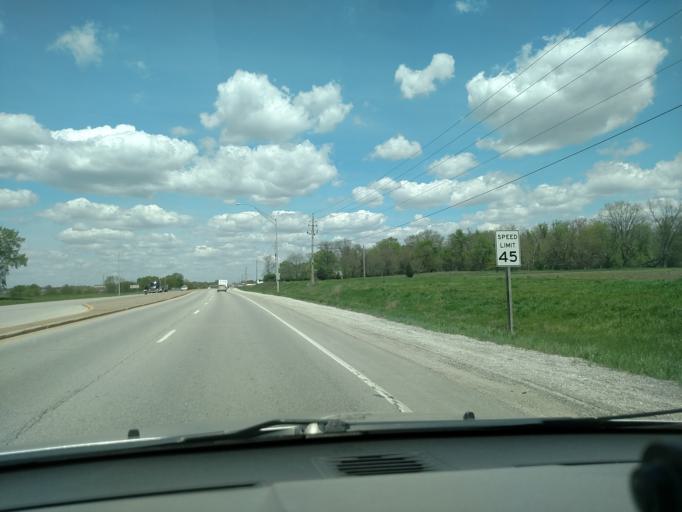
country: US
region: Iowa
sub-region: Polk County
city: Ankeny
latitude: 41.7035
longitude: -93.6004
